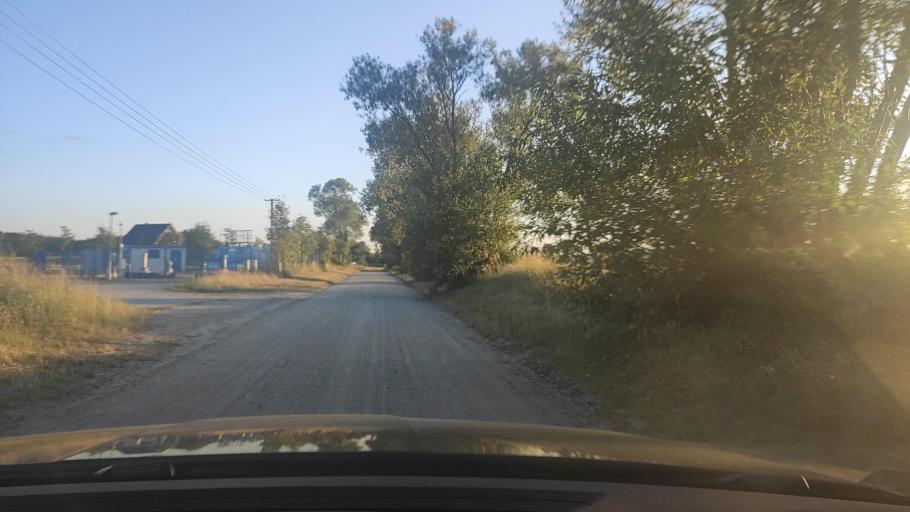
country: PL
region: Greater Poland Voivodeship
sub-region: Powiat poznanski
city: Kobylnica
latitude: 52.4593
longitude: 17.1614
